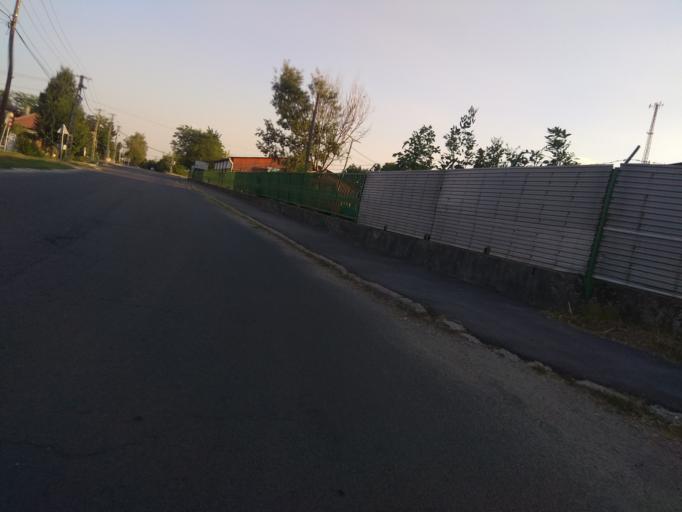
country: HU
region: Borsod-Abauj-Zemplen
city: Nyekladhaza
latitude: 47.9884
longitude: 20.8336
